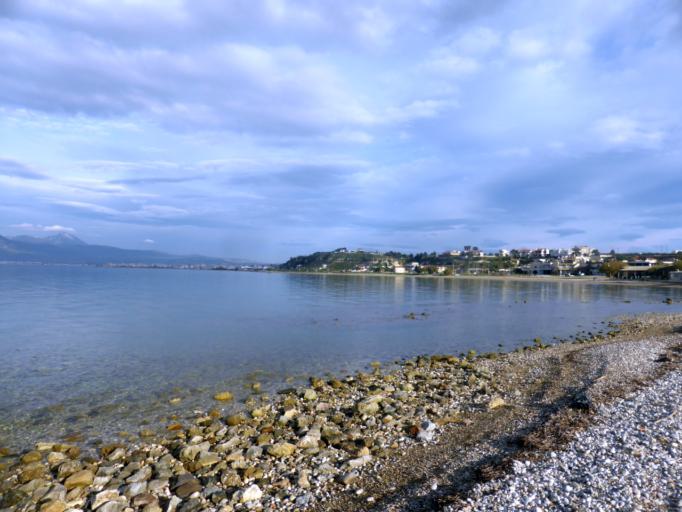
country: GR
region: Peloponnese
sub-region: Nomos Korinthias
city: Arkhaia Korinthos
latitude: 37.9331
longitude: 22.8935
